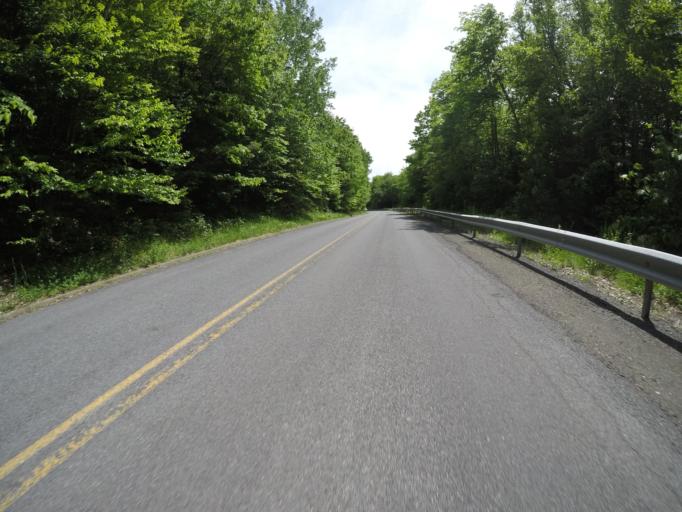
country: US
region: New York
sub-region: Delaware County
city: Delhi
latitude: 42.1145
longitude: -74.8206
